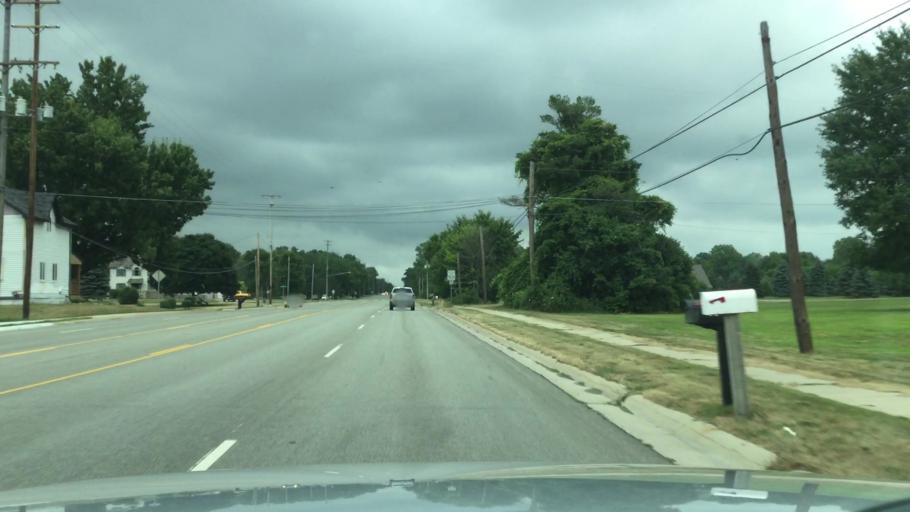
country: US
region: Michigan
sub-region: Genesee County
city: Burton
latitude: 43.0335
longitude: -83.5758
